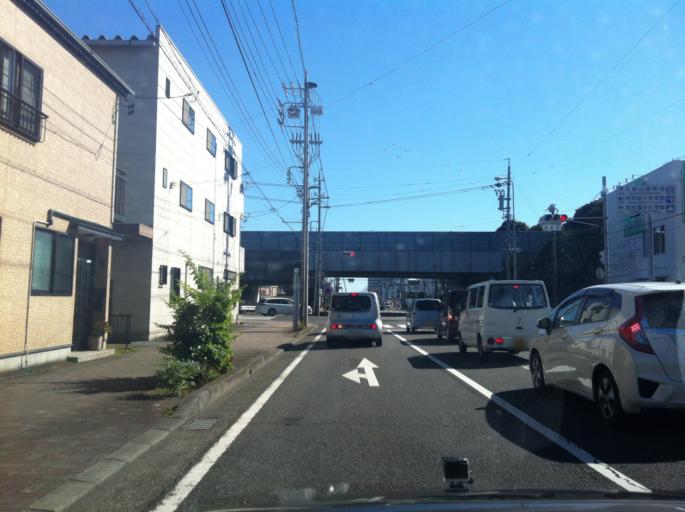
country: JP
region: Shizuoka
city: Shizuoka-shi
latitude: 34.9527
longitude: 138.4069
